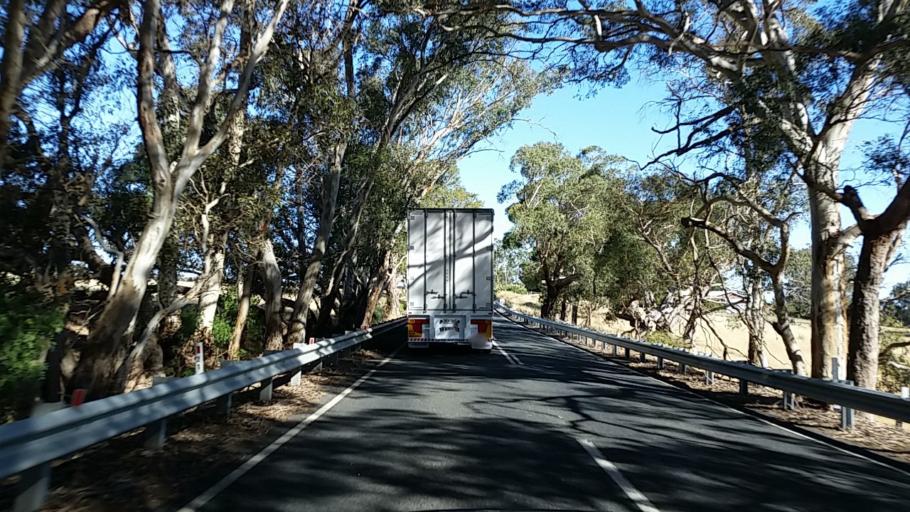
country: AU
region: South Australia
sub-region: Adelaide Hills
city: Birdwood
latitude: -34.7678
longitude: 139.0208
